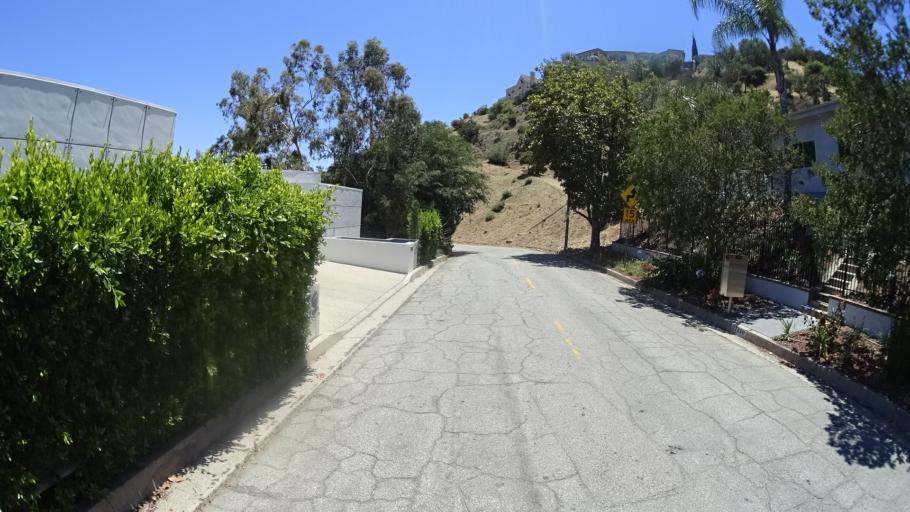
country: US
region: California
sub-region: Los Angeles County
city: Universal City
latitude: 34.1180
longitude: -118.3695
